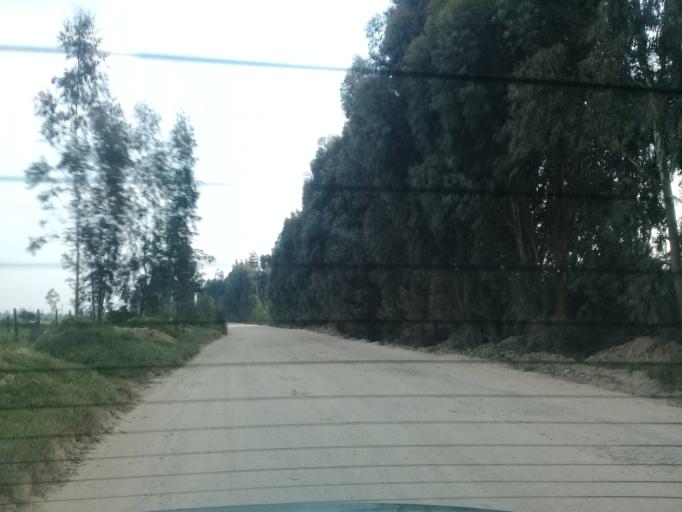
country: CO
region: Cundinamarca
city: Funza
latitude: 4.7735
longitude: -74.2211
